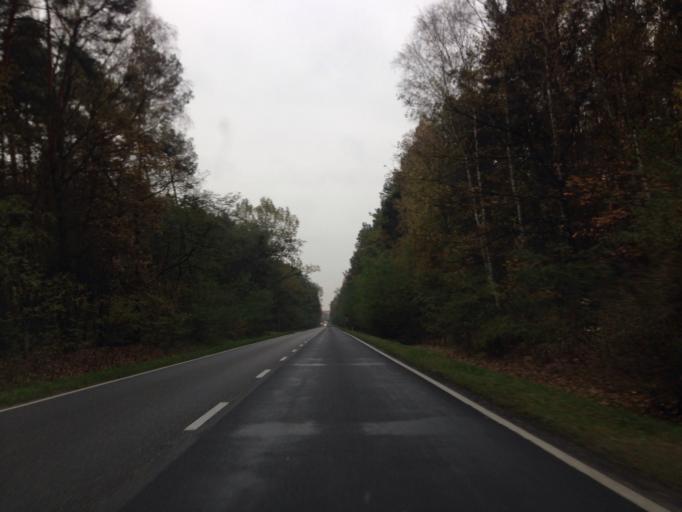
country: PL
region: Masovian Voivodeship
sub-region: Powiat warszawski zachodni
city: Leszno
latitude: 52.2679
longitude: 20.5943
